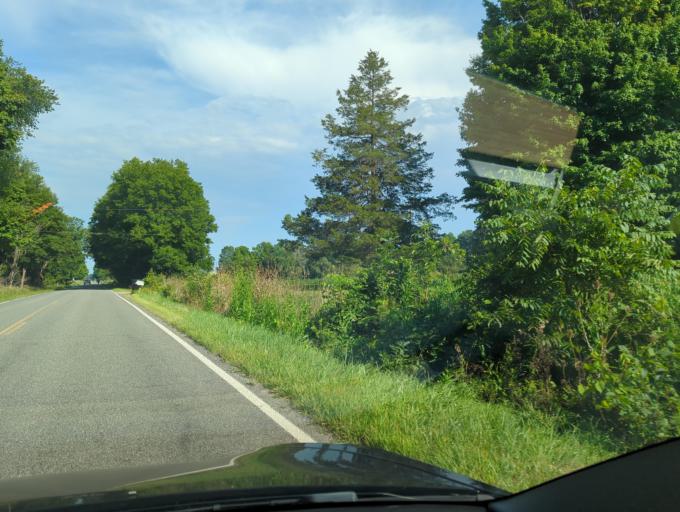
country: US
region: Michigan
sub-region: Ionia County
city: Ionia
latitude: 42.9296
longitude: -85.1178
